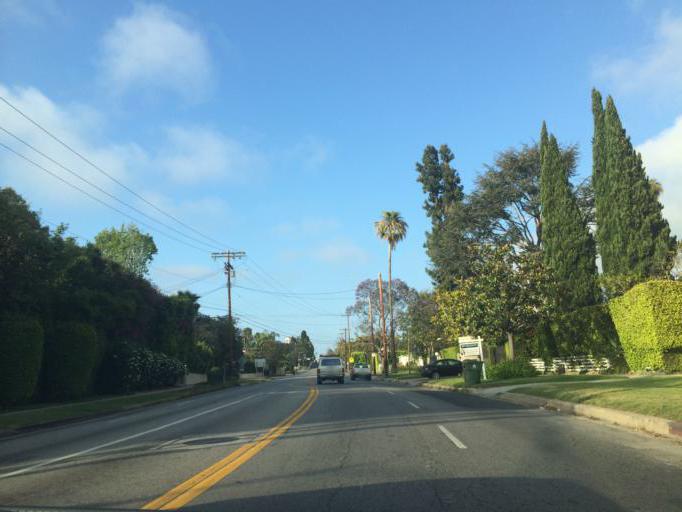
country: US
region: California
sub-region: Los Angeles County
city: Santa Monica
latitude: 34.0585
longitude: -118.4782
